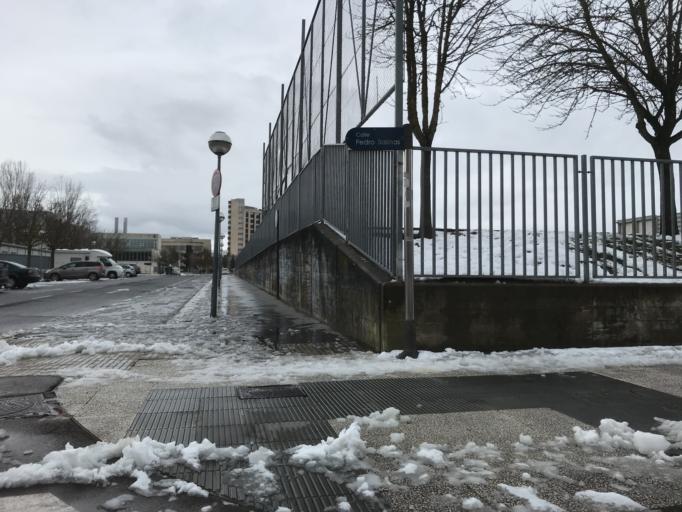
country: ES
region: Basque Country
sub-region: Provincia de Alava
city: Gasteiz / Vitoria
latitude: 42.8614
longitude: -2.6906
